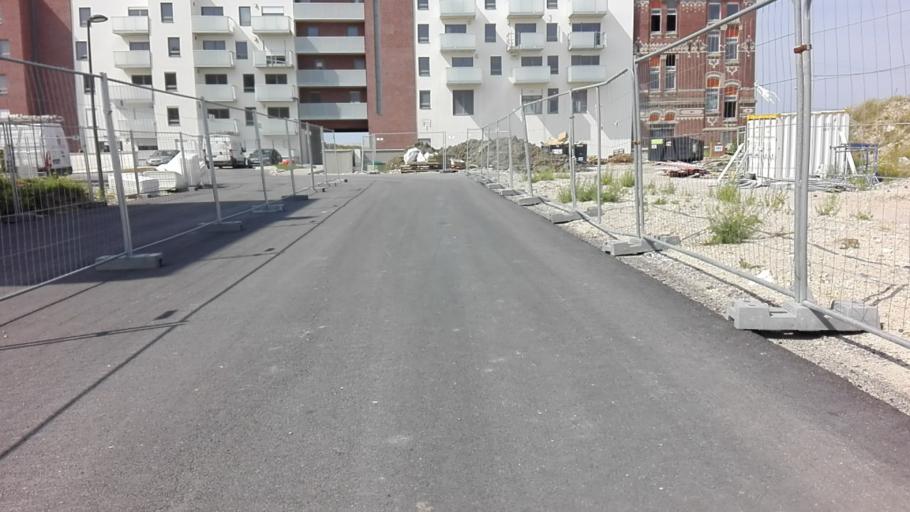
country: FR
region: Nord-Pas-de-Calais
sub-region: Departement du Pas-de-Calais
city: Berck-Plage
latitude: 50.4022
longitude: 1.5589
